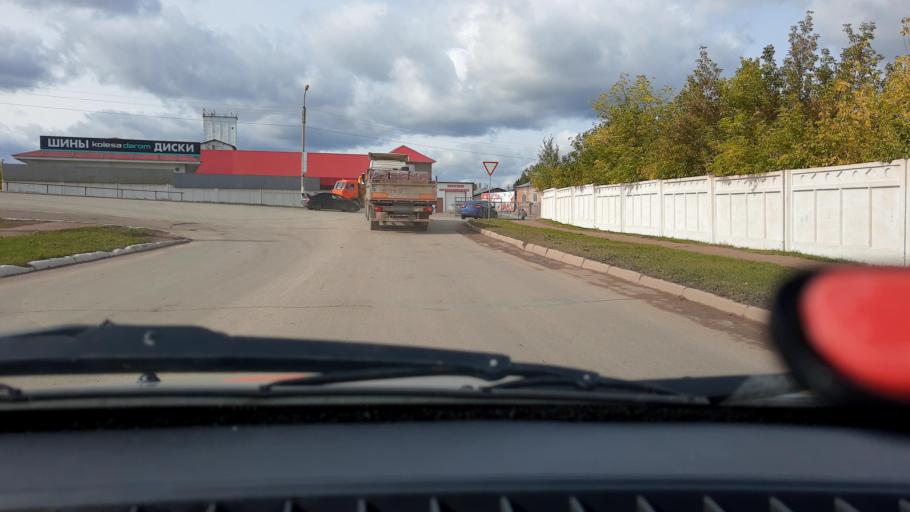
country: RU
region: Bashkortostan
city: Belebey
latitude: 54.0975
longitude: 54.1238
